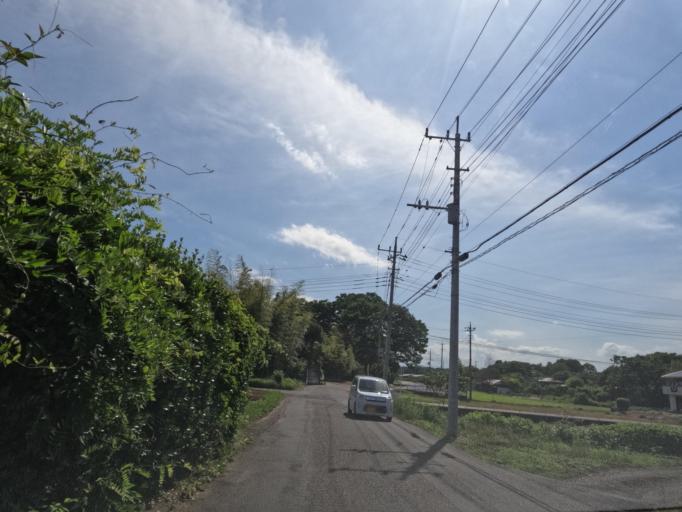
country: JP
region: Saitama
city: Kumagaya
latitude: 36.1018
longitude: 139.3792
